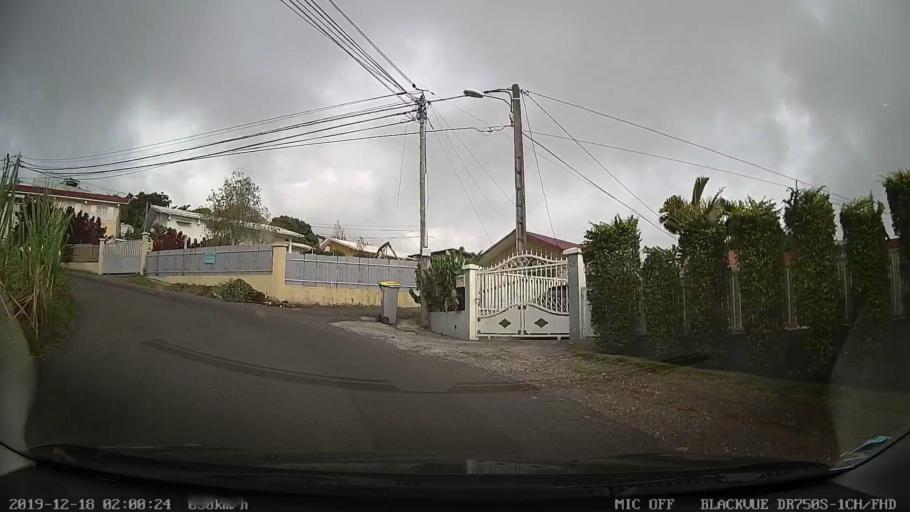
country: RE
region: Reunion
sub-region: Reunion
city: Le Tampon
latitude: -21.2535
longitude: 55.5179
